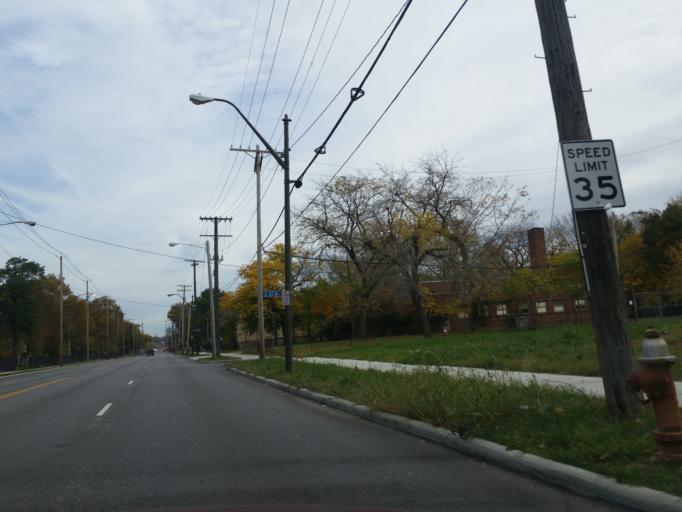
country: US
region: Ohio
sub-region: Cuyahoga County
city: Newburgh Heights
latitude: 41.4879
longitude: -81.6443
